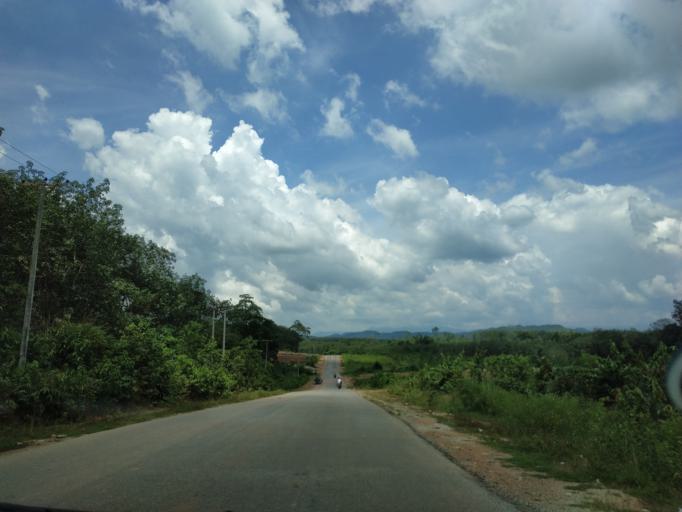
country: TH
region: Kanchanaburi
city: Sangkhla Buri
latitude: 15.2707
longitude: 97.8587
